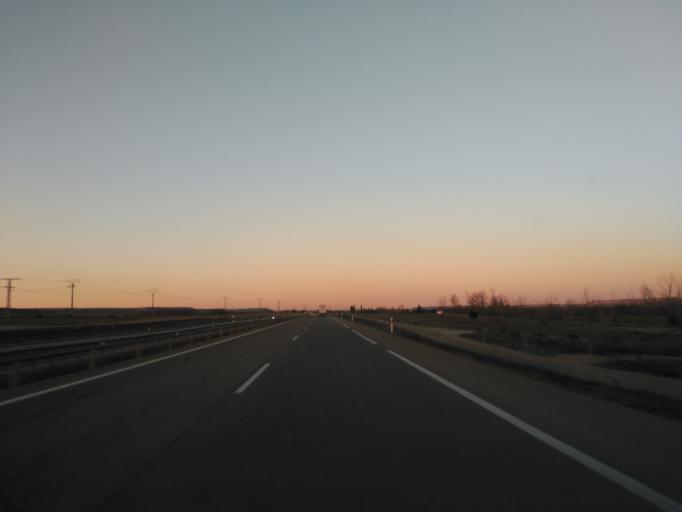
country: ES
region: Castille and Leon
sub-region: Provincia de Valladolid
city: Cubillas de Santa Marta
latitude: 41.7847
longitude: -4.6106
